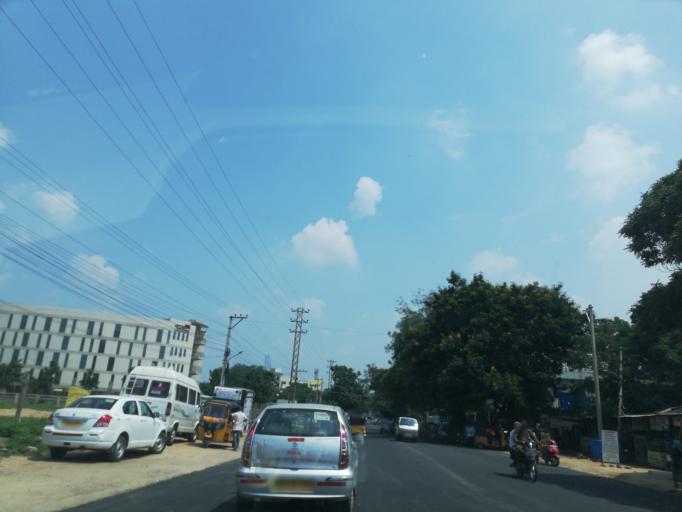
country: IN
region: Telangana
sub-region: Medak
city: Serilingampalle
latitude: 17.4807
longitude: 78.3201
